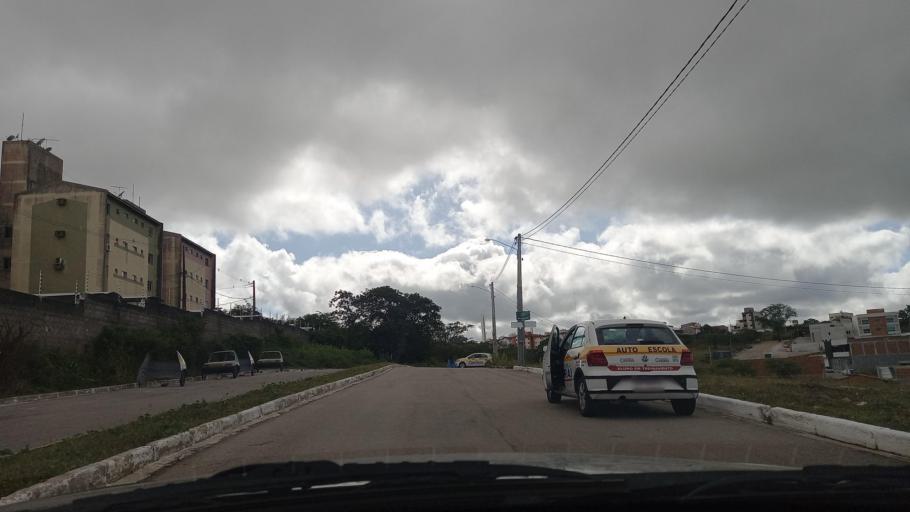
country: BR
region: Pernambuco
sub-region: Caruaru
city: Caruaru
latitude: -8.3026
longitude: -35.9587
